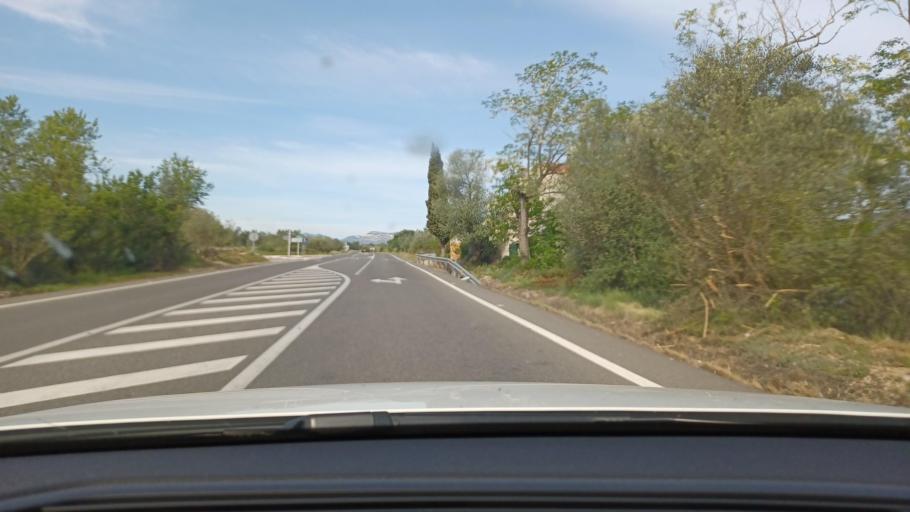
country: ES
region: Catalonia
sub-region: Provincia de Tarragona
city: Mas de Barberans
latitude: 40.6412
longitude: 0.3551
